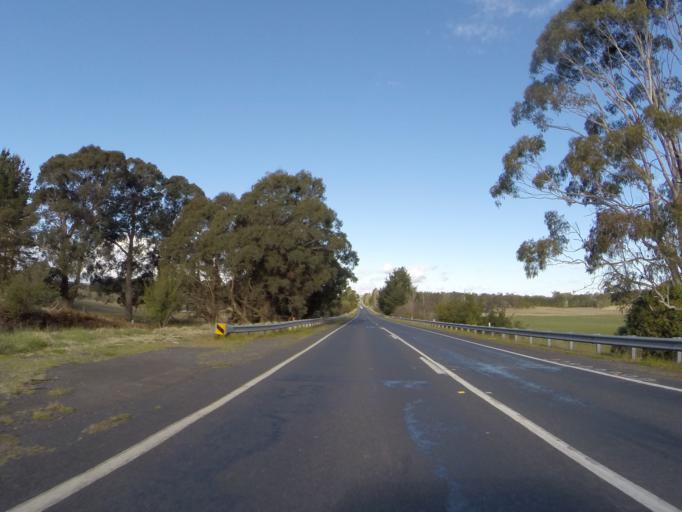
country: AU
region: New South Wales
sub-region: Wingecarribee
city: Moss Vale
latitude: -34.5674
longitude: 150.4258
